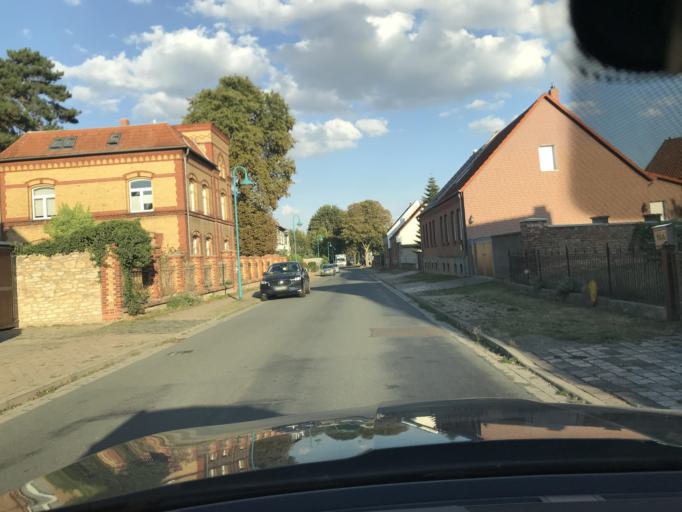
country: DE
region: Saxony-Anhalt
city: Schwanebeck
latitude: 51.9636
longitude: 11.1263
